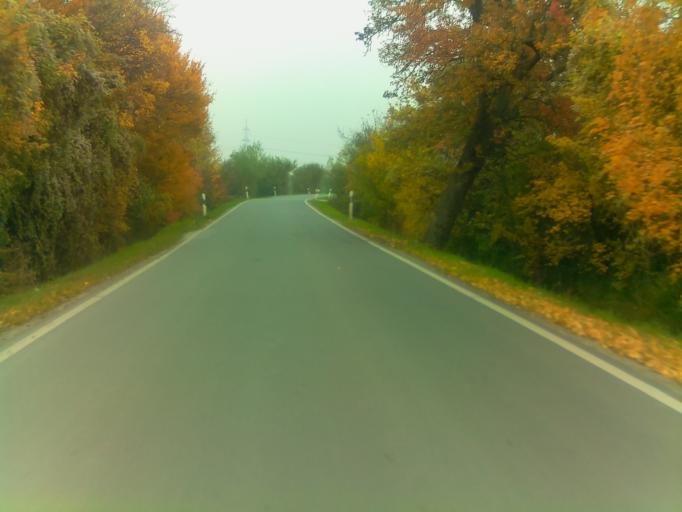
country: DE
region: Rheinland-Pfalz
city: Fussgonheim
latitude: 49.4638
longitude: 8.2972
